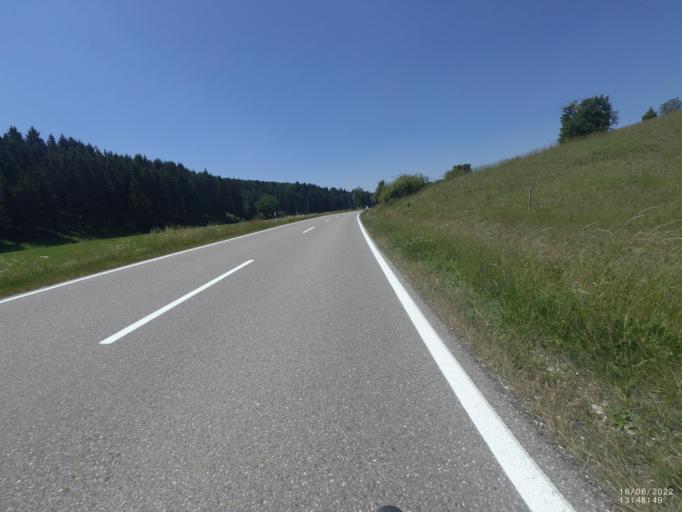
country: DE
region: Baden-Wuerttemberg
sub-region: Tuebingen Region
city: Ballendorf
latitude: 48.5844
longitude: 10.0774
